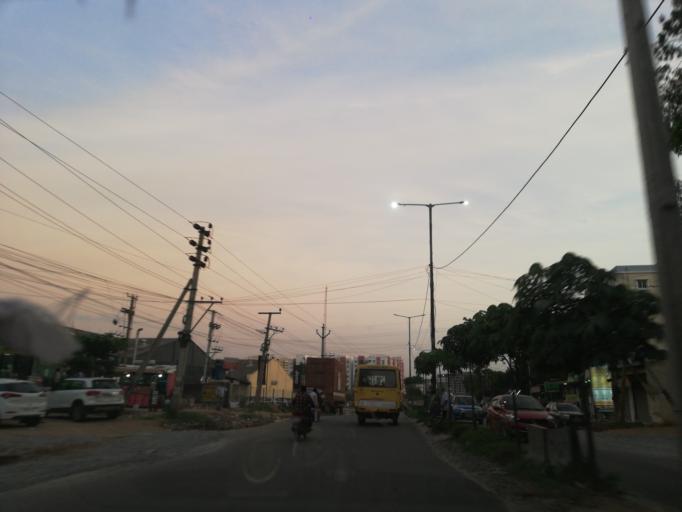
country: IN
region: Telangana
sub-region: Rangareddi
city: Kukatpalli
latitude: 17.5099
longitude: 78.3619
